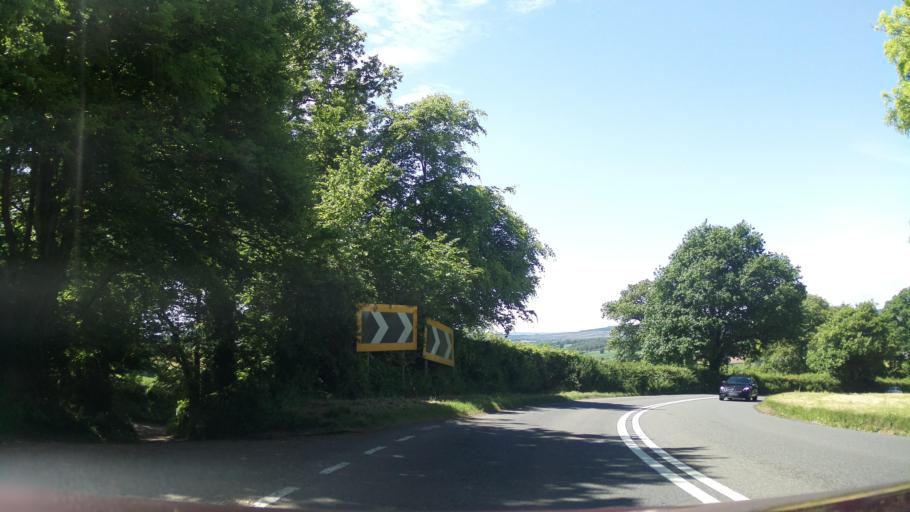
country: GB
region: England
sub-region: Devon
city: Newton Poppleford
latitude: 50.6985
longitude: -3.2742
